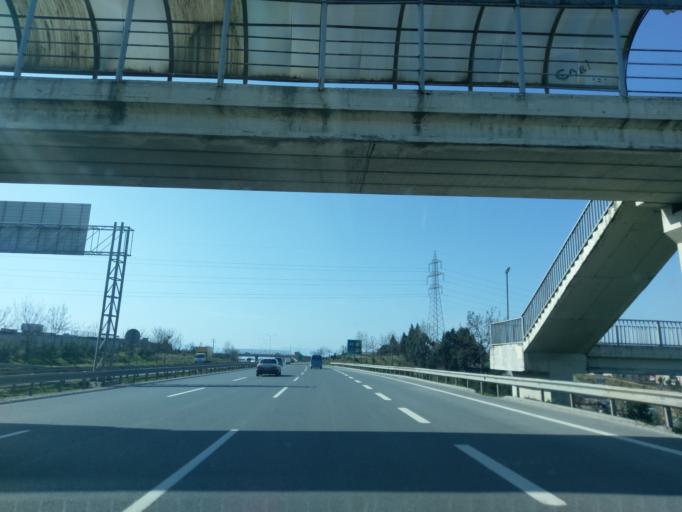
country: TR
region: Kocaeli
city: Balcik
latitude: 40.8607
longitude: 29.3799
